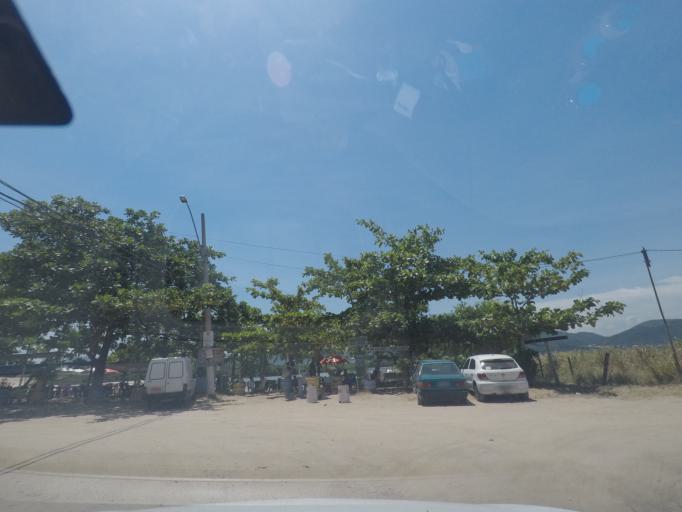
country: BR
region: Rio de Janeiro
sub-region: Niteroi
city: Niteroi
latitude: -22.9670
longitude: -43.0443
